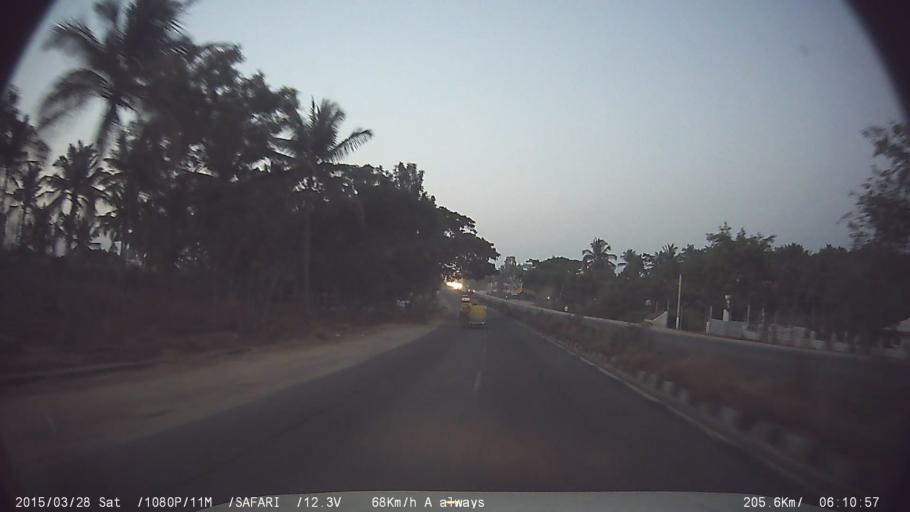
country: IN
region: Karnataka
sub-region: Ramanagara
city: Ramanagaram
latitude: 12.7875
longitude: 77.3742
